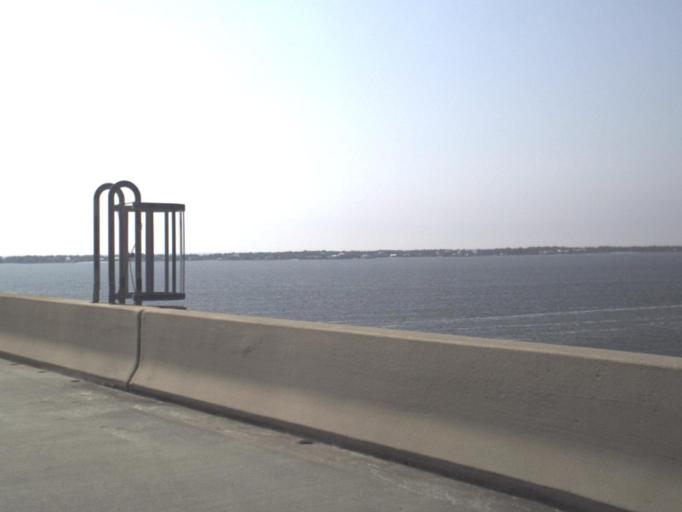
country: US
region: Florida
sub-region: Franklin County
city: Eastpoint
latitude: 29.6841
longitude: -84.8808
